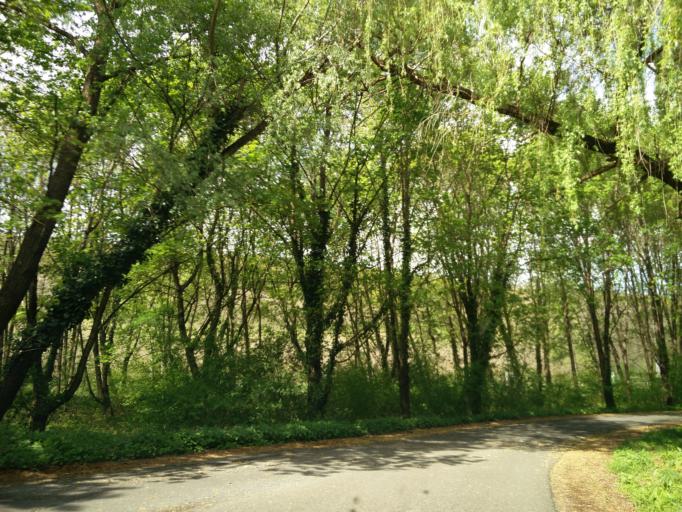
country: HU
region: Zala
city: Zalaegerszeg
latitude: 46.8070
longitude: 16.8264
